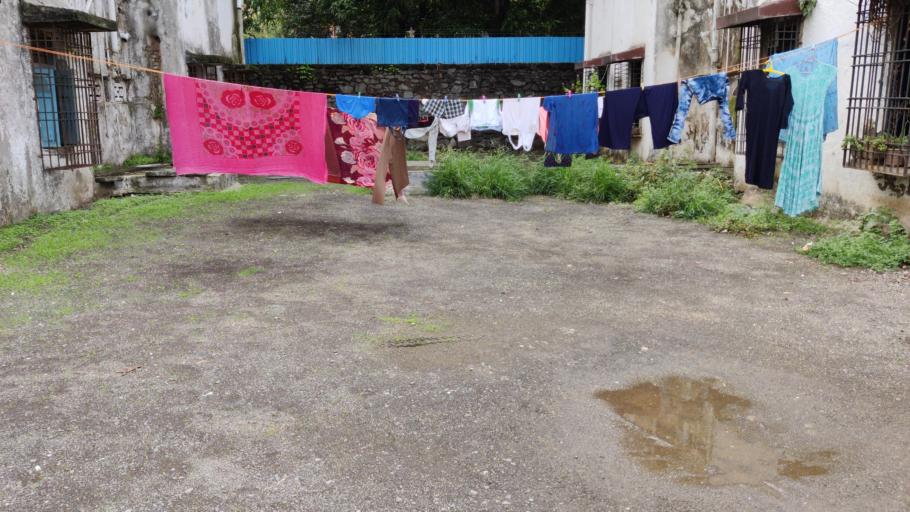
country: IN
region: Maharashtra
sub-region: Mumbai Suburban
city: Borivli
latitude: 19.2450
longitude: 72.8595
